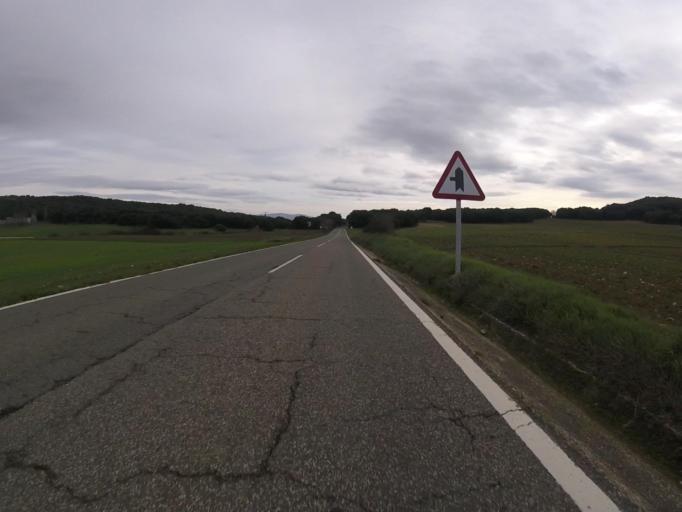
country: ES
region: Navarre
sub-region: Provincia de Navarra
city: Lezaun
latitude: 42.7394
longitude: -2.0190
